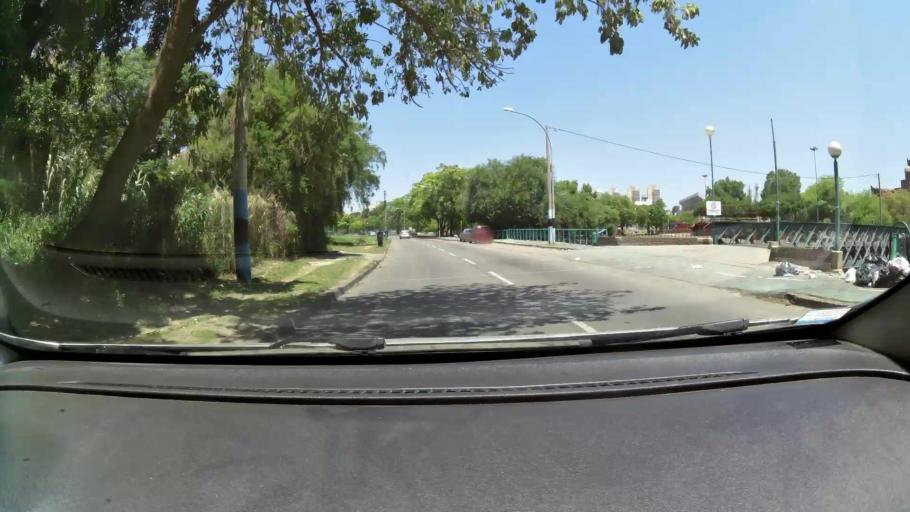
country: AR
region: Cordoba
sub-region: Departamento de Capital
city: Cordoba
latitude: -31.4011
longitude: -64.2038
